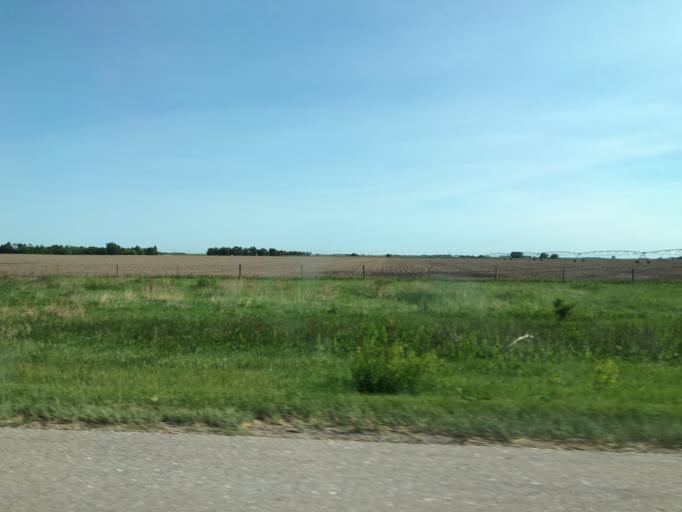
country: US
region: Nebraska
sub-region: Seward County
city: Seward
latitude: 40.8222
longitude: -97.1635
